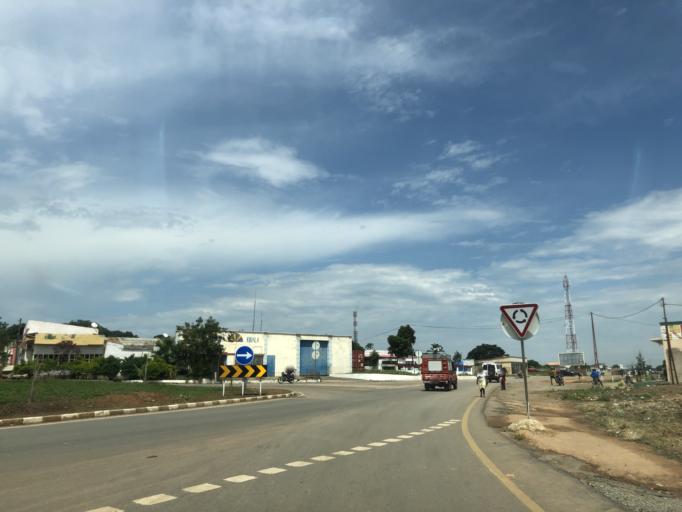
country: AO
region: Cuanza Sul
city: Quibala
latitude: -10.7357
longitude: 14.9825
